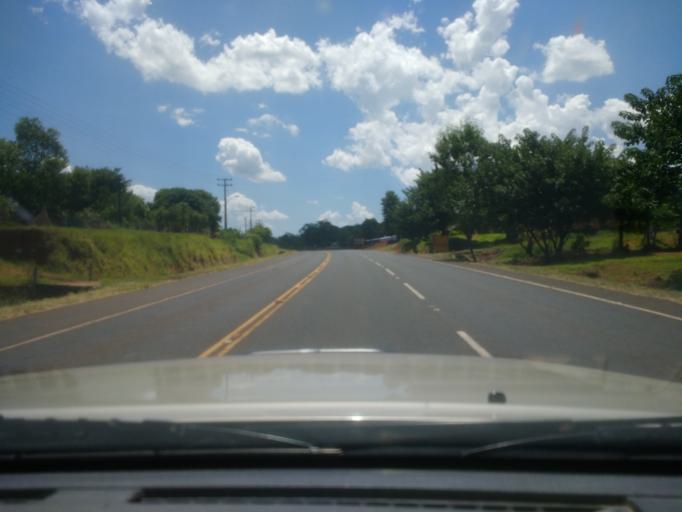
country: PY
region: San Pedro
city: Guayaybi
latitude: -24.5958
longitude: -56.5081
